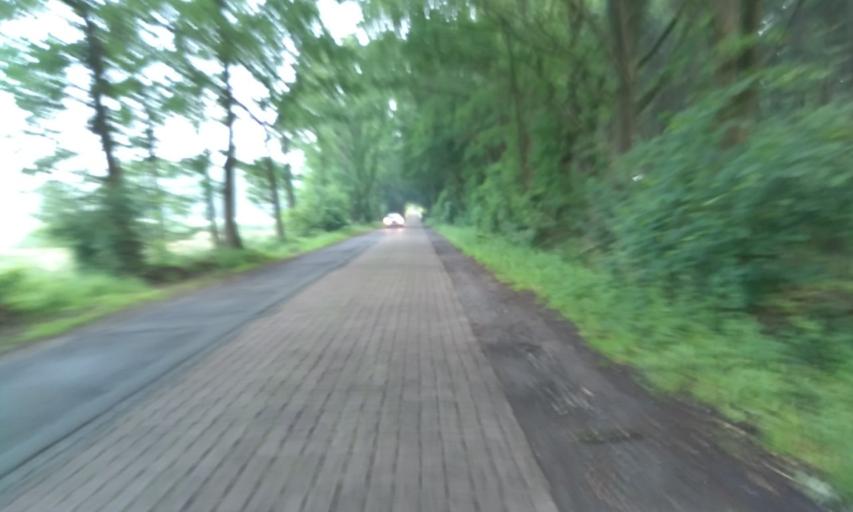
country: DE
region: Lower Saxony
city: Deinste
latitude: 53.5052
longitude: 9.4526
